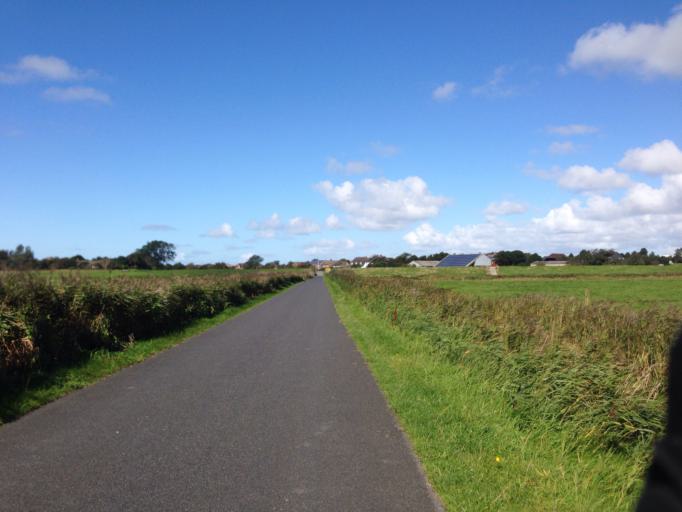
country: DE
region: Schleswig-Holstein
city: Witsum
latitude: 54.7014
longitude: 8.4226
